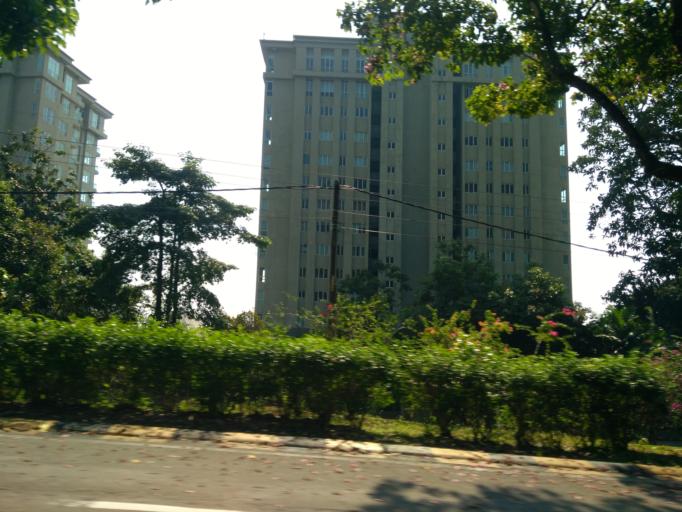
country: MY
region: Sarawak
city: Kuching
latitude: 1.7339
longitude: 110.3156
